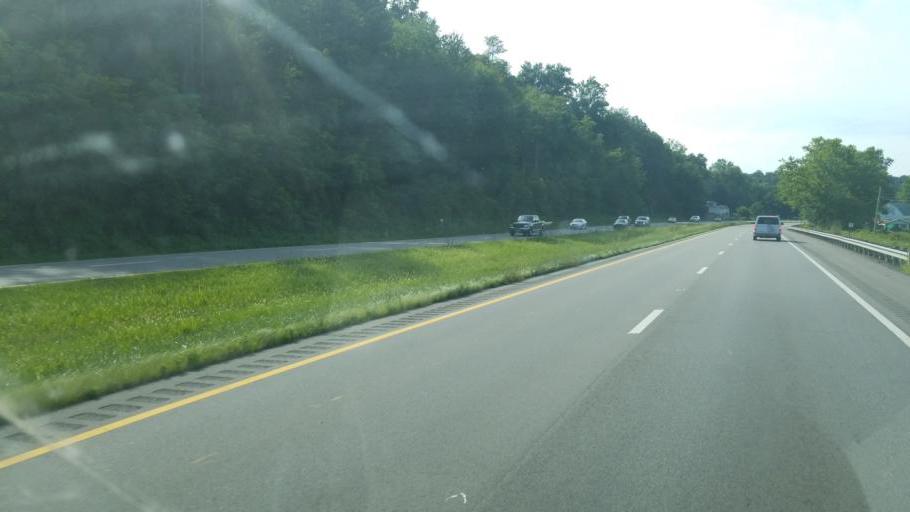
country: US
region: Ohio
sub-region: Hocking County
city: Logan
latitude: 39.5718
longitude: -82.5186
